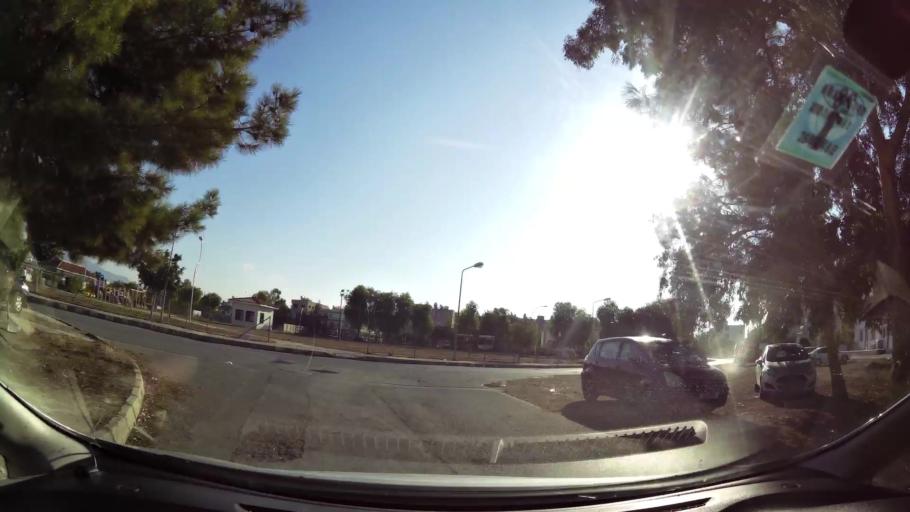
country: CY
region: Lefkosia
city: Nicosia
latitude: 35.2046
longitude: 33.3493
